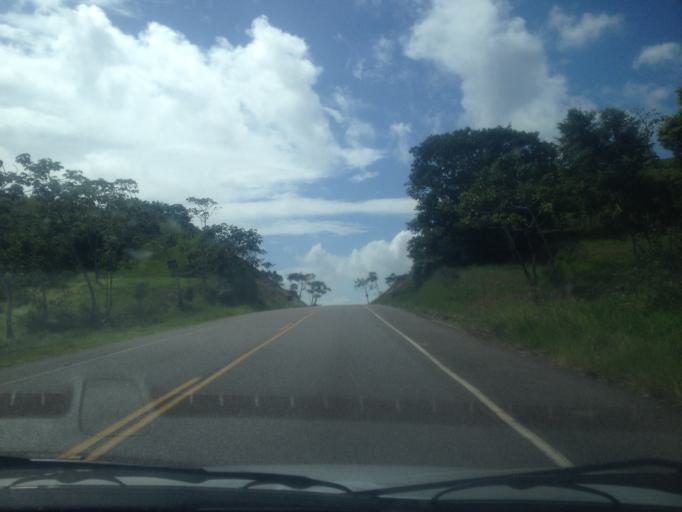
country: BR
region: Bahia
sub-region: Conde
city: Conde
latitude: -11.7801
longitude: -37.6137
